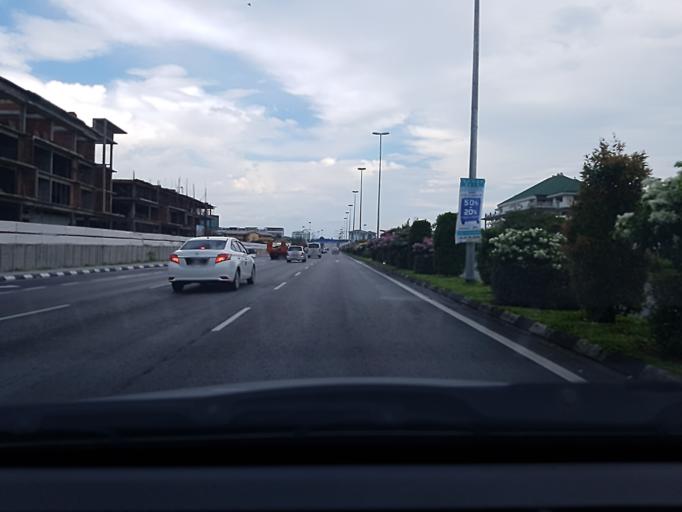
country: MY
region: Sarawak
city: Kuching
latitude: 1.5110
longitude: 110.3520
